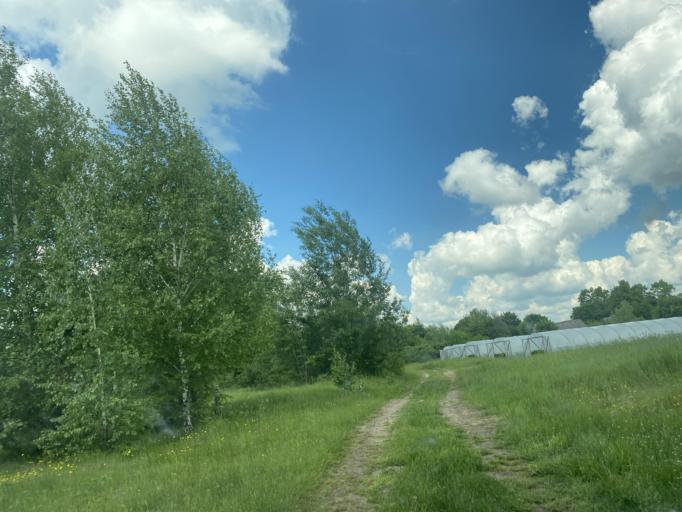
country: BY
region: Brest
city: Ivanava
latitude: 52.2021
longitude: 25.6108
